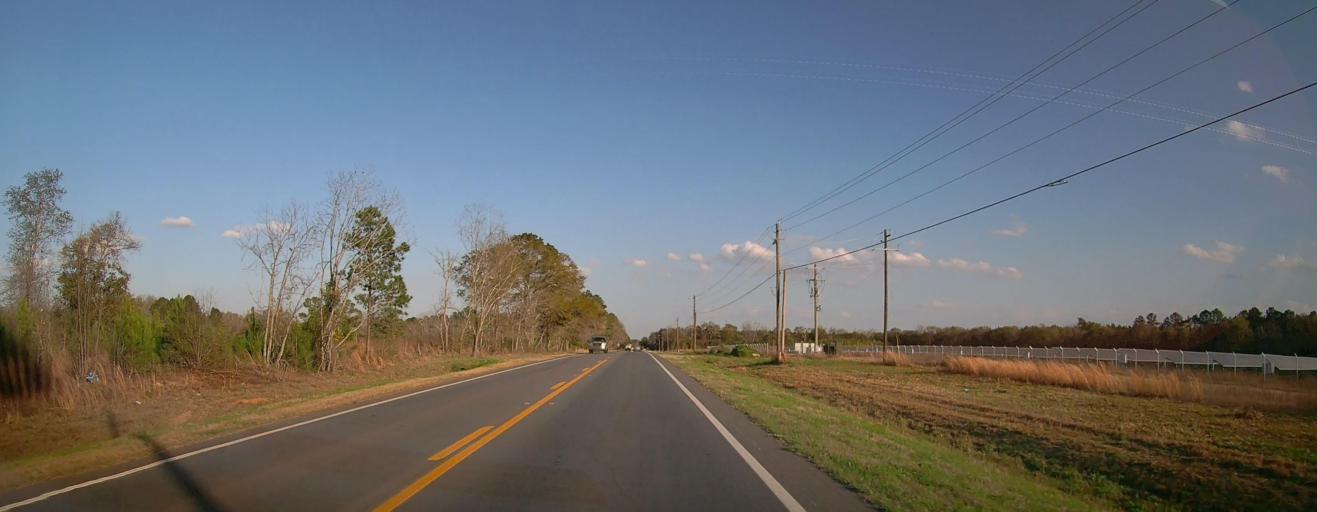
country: US
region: Georgia
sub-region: Evans County
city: Claxton
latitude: 32.1580
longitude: -81.8598
